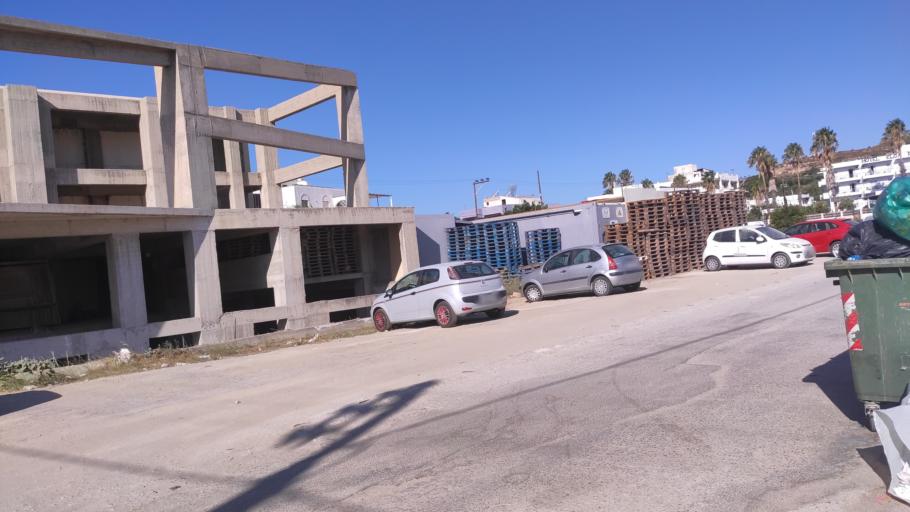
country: GR
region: South Aegean
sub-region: Nomos Dodekanisou
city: Kardamaina
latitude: 36.7835
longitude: 27.1428
